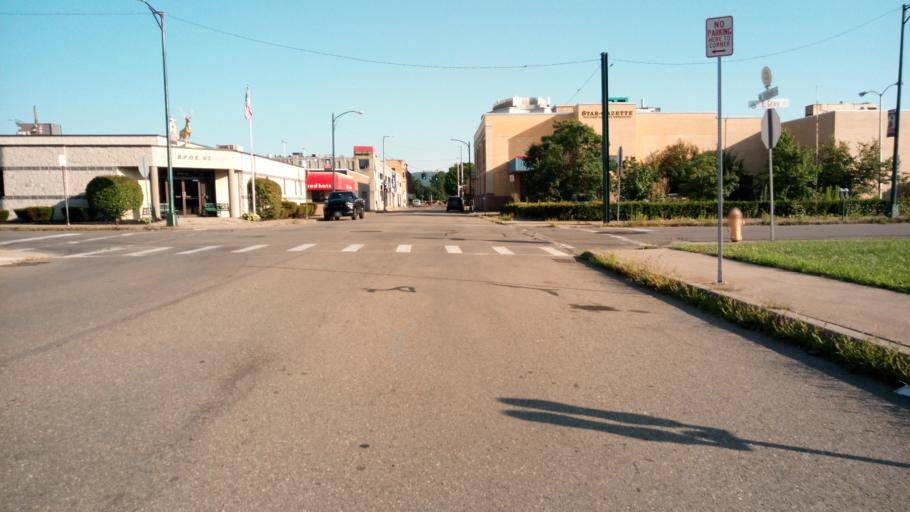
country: US
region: New York
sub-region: Chemung County
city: Elmira
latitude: 42.0903
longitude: -76.8038
